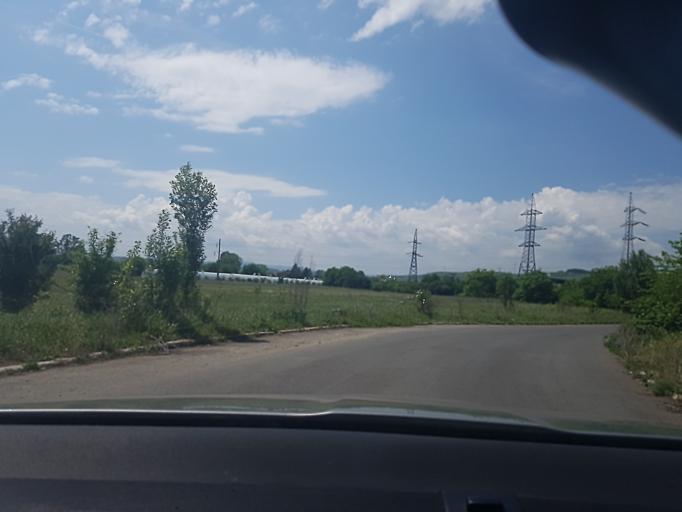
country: RO
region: Hunedoara
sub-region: Comuna Calan
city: Calan
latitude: 45.7386
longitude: 23.0029
